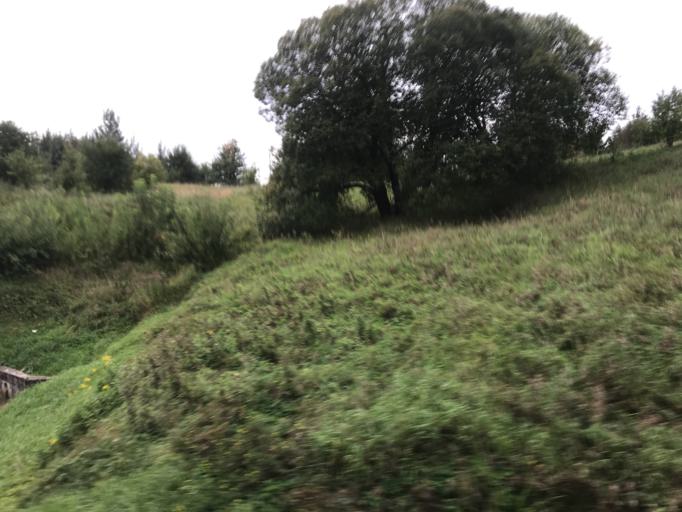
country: LT
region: Vilnius County
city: Vilkpede
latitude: 54.6569
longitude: 25.2658
